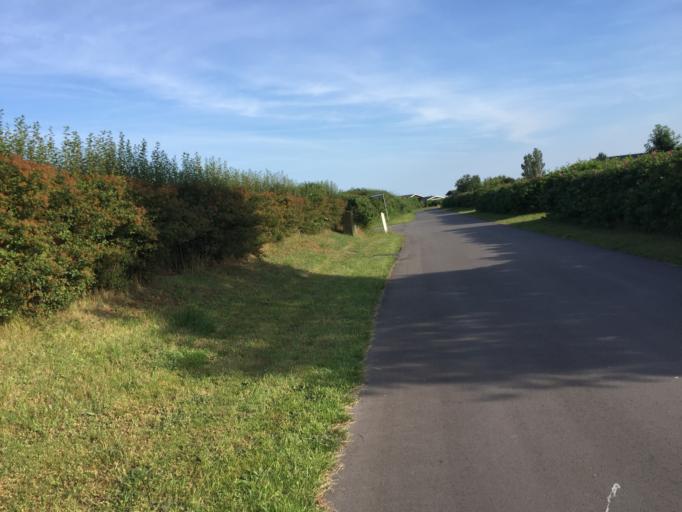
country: DK
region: South Denmark
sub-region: Assens Kommune
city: Harby
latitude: 55.1267
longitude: 10.0301
